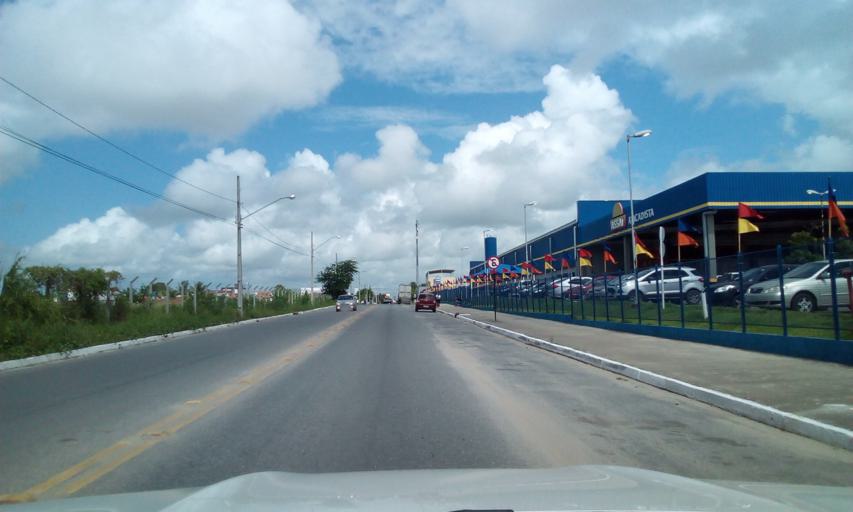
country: BR
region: Paraiba
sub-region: Joao Pessoa
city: Joao Pessoa
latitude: -7.1715
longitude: -34.8683
